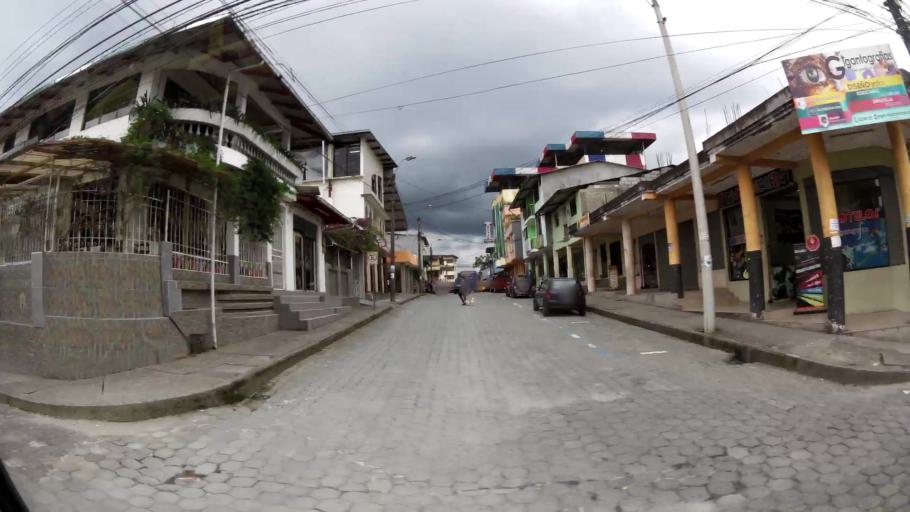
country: EC
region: Pastaza
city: Puyo
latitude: -1.4878
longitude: -77.9964
